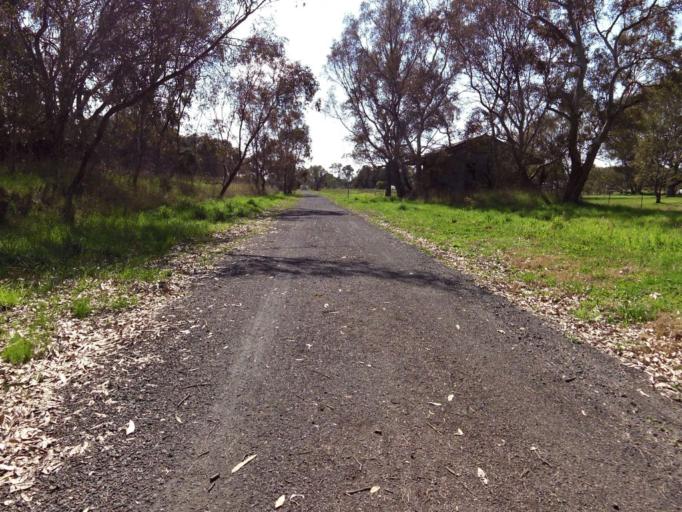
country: AU
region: Victoria
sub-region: Murrindindi
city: Alexandra
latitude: -37.1051
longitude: 145.6164
